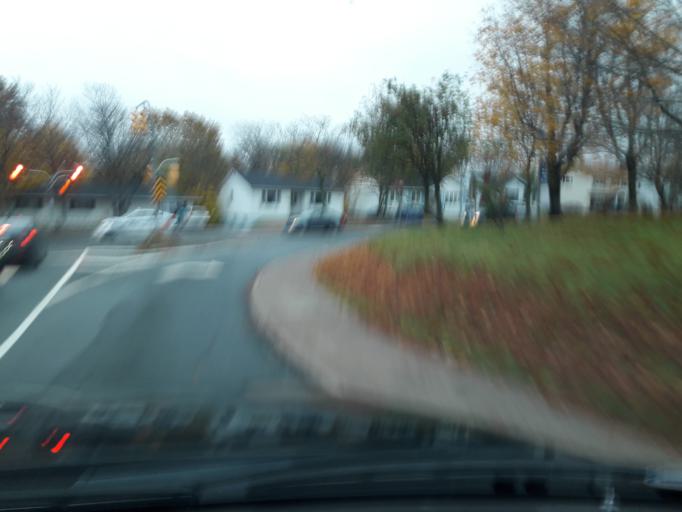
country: CA
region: Newfoundland and Labrador
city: St. John's
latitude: 47.5690
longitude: -52.7344
